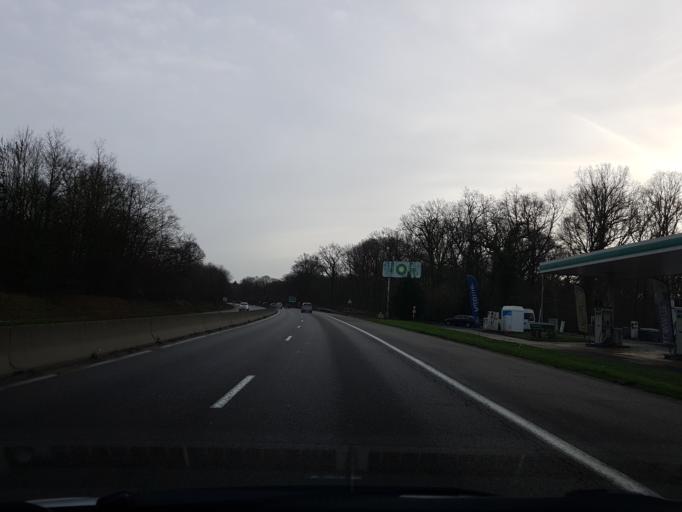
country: FR
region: Ile-de-France
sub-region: Departement de l'Essonne
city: Montgeron
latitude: 48.6909
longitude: 2.4541
